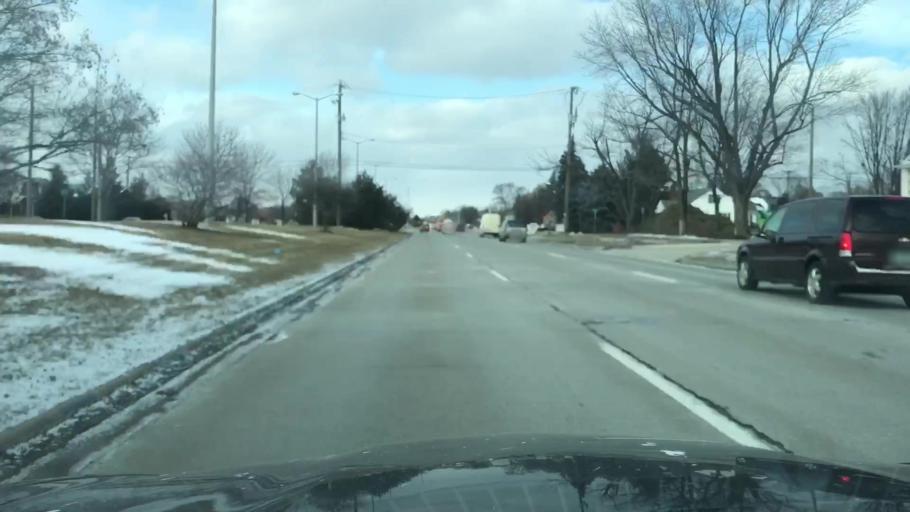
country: US
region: Michigan
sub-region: Macomb County
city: Utica
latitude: 42.6192
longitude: -83.0517
